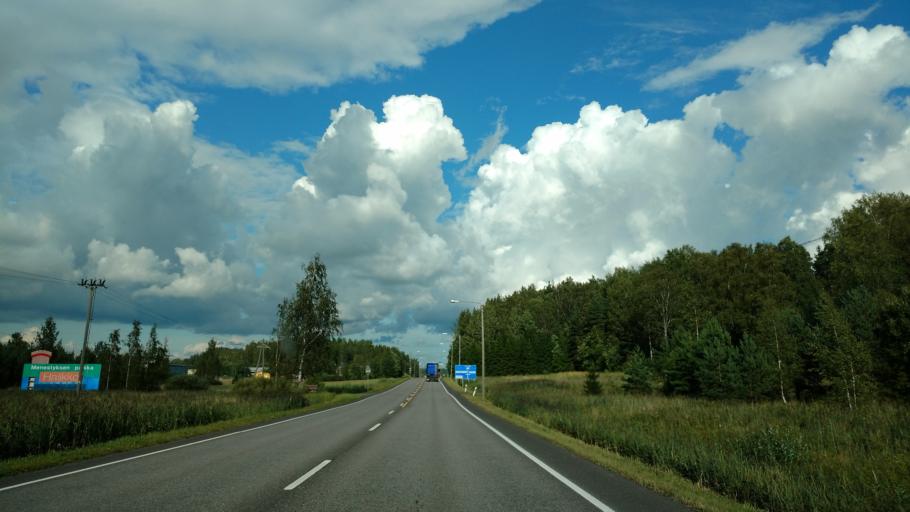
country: FI
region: Varsinais-Suomi
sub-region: Salo
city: Halikko
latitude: 60.3816
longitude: 23.0345
